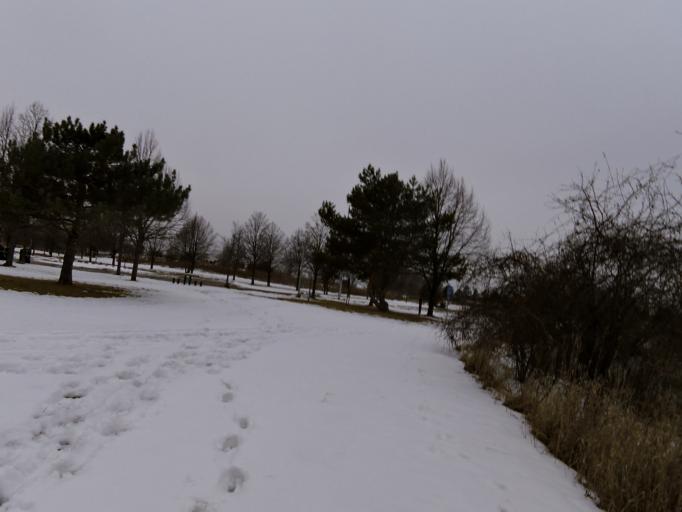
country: US
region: Minnesota
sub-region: Washington County
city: Lakeland
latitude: 44.9523
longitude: -92.8207
